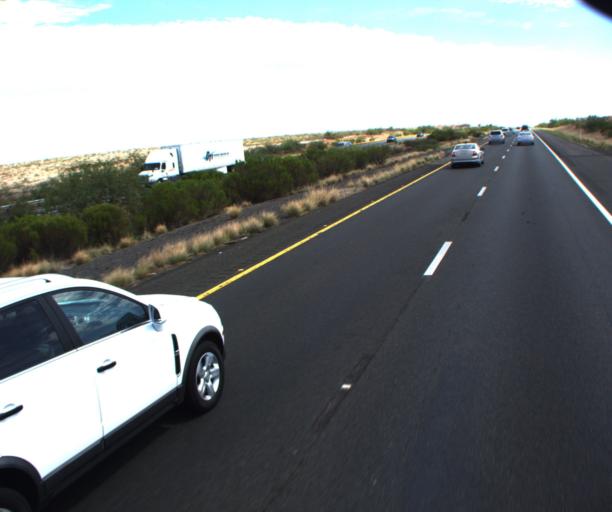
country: US
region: Arizona
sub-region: Yavapai County
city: Spring Valley
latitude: 34.3673
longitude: -112.1134
